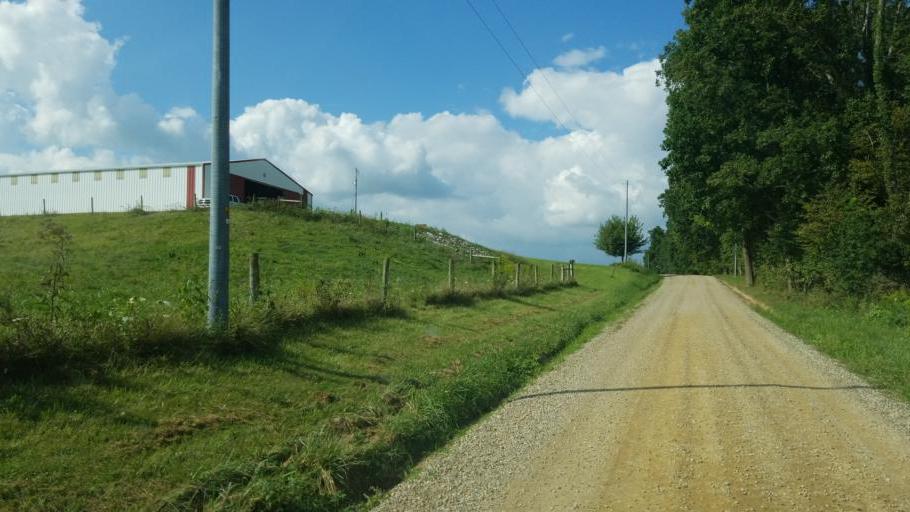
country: US
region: Ohio
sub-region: Knox County
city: Danville
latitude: 40.4532
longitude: -82.3082
